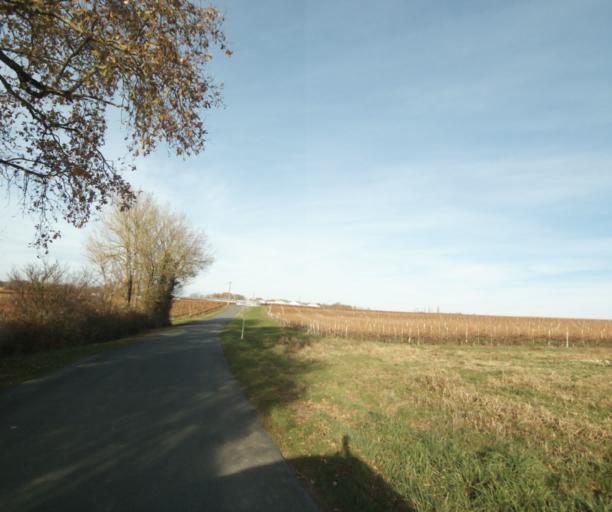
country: FR
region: Poitou-Charentes
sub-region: Departement de la Charente-Maritime
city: Chaniers
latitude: 45.7312
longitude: -0.5270
